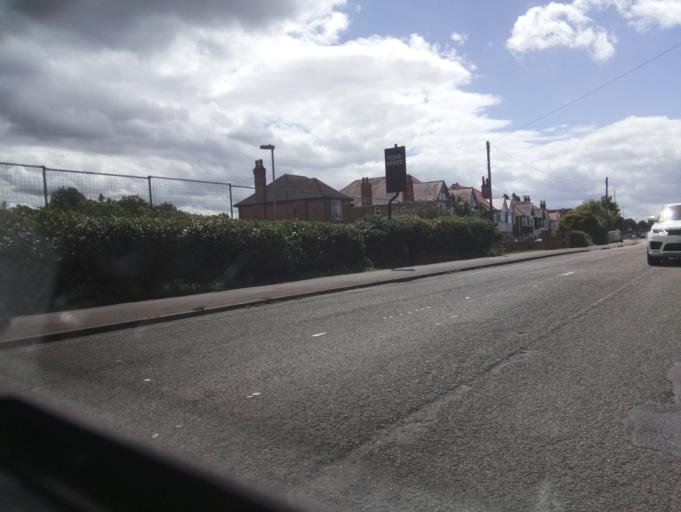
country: GB
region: England
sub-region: Nottinghamshire
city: Arnold
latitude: 52.9893
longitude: -1.1136
